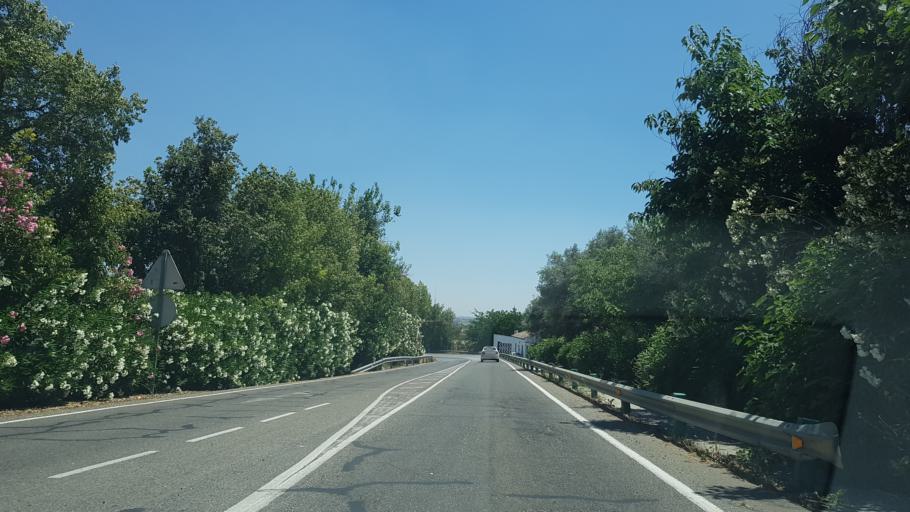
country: ES
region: Andalusia
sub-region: Provincia de Sevilla
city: Tomares
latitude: 37.3850
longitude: -6.0365
